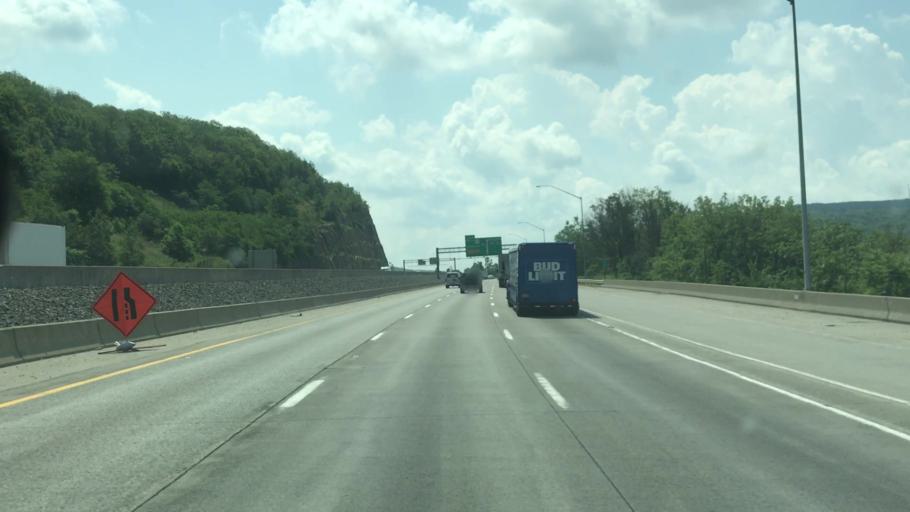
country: US
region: Pennsylvania
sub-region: Lackawanna County
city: Dunmore
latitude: 41.4073
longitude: -75.5934
